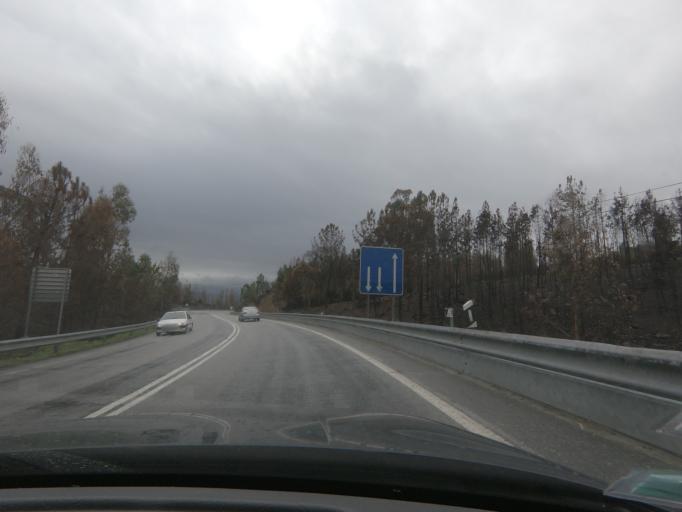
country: PT
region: Braga
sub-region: Celorico de Basto
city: Celorico de Basto
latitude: 41.3469
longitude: -8.0261
